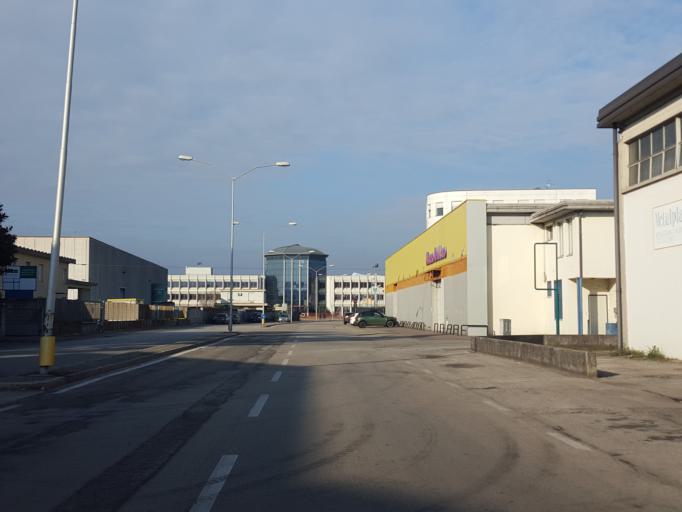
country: IT
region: Veneto
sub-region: Provincia di Vicenza
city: Creazzo
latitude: 45.5277
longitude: 11.5122
